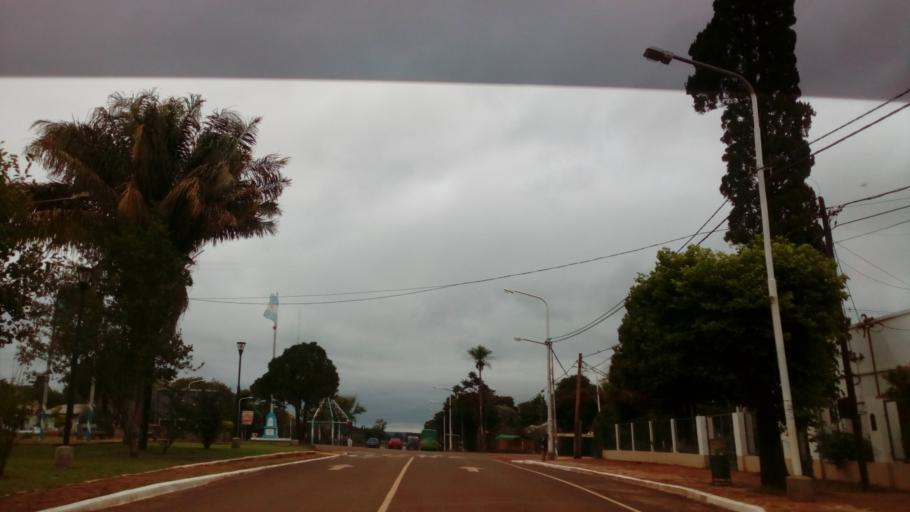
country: AR
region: Misiones
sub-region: Departamento de Candelaria
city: Candelaria
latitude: -27.4611
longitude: -55.7449
